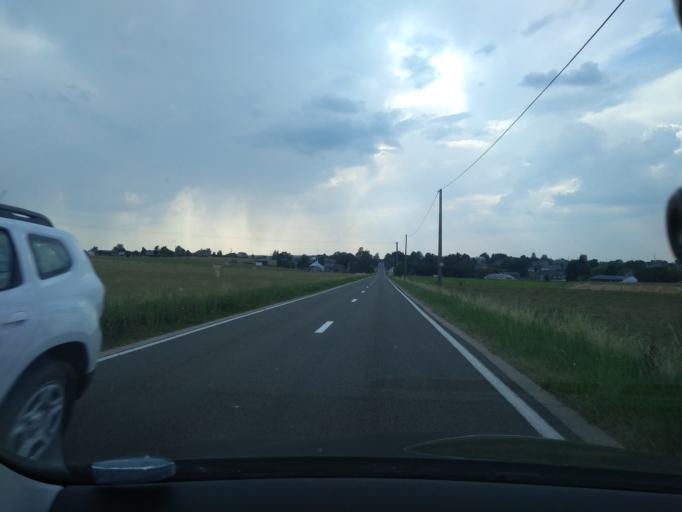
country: BE
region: Wallonia
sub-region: Province du Luxembourg
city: Bertogne
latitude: 50.0806
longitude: 5.6762
